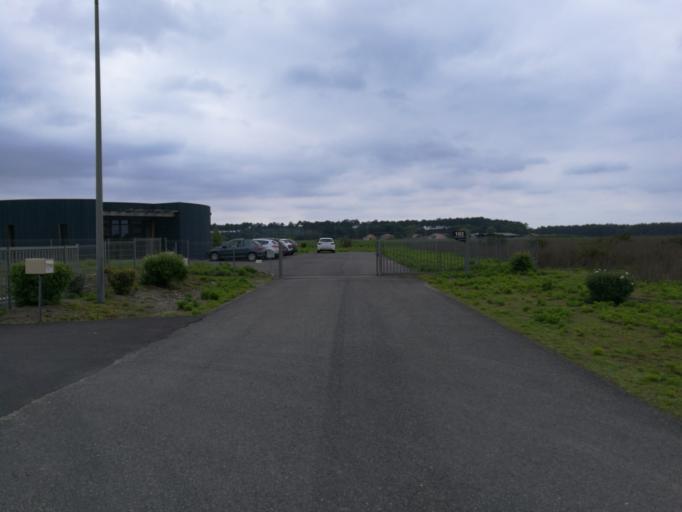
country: FR
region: Aquitaine
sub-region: Departement des Landes
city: Saint-Geours-de-Maremne
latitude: 43.7116
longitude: -1.2378
